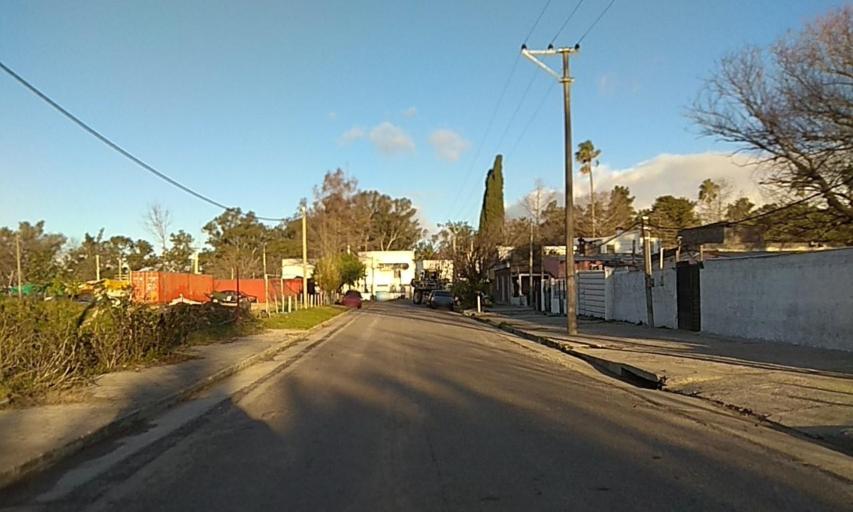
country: UY
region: Florida
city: Florida
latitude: -34.0959
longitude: -56.2076
